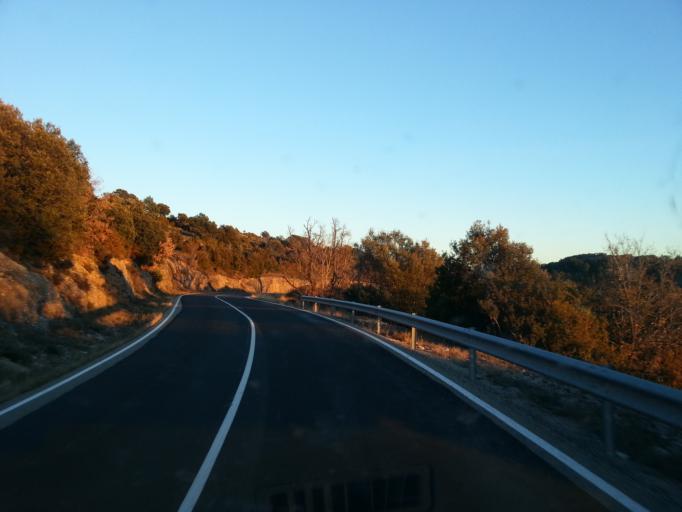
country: ES
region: Catalonia
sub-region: Provincia de Lleida
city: Olius
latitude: 42.1143
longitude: 1.5431
